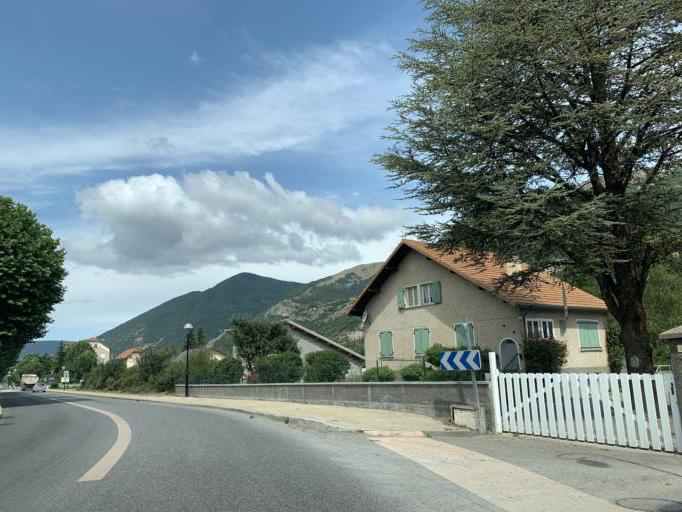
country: FR
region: Provence-Alpes-Cote d'Azur
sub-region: Departement des Hautes-Alpes
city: La Roche-des-Arnauds
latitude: 44.5618
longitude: 5.9555
